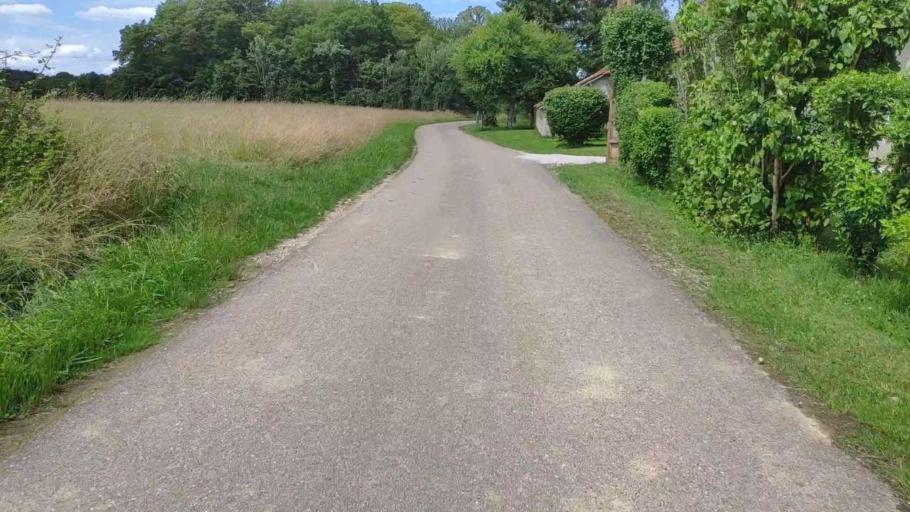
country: FR
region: Franche-Comte
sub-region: Departement du Jura
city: Chaussin
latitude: 46.8825
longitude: 5.4025
